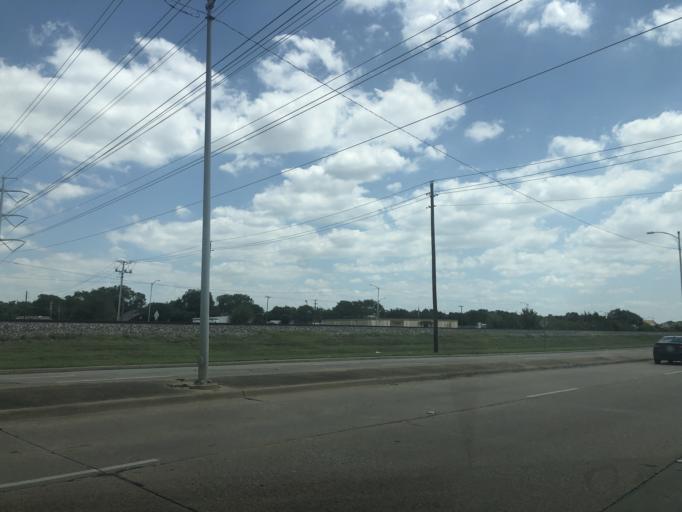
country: US
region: Texas
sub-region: Dallas County
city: Grand Prairie
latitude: 32.7392
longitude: -97.0346
